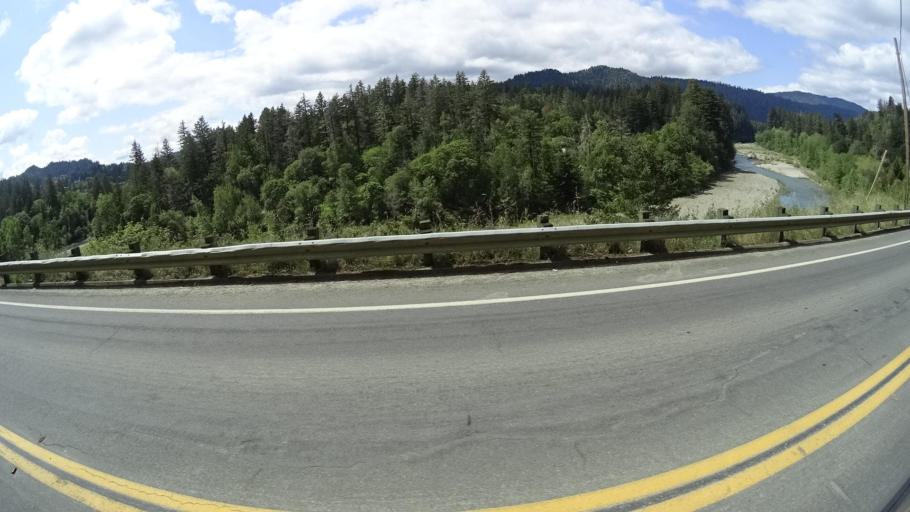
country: US
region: California
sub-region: Humboldt County
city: Redway
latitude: 40.1166
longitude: -123.7969
